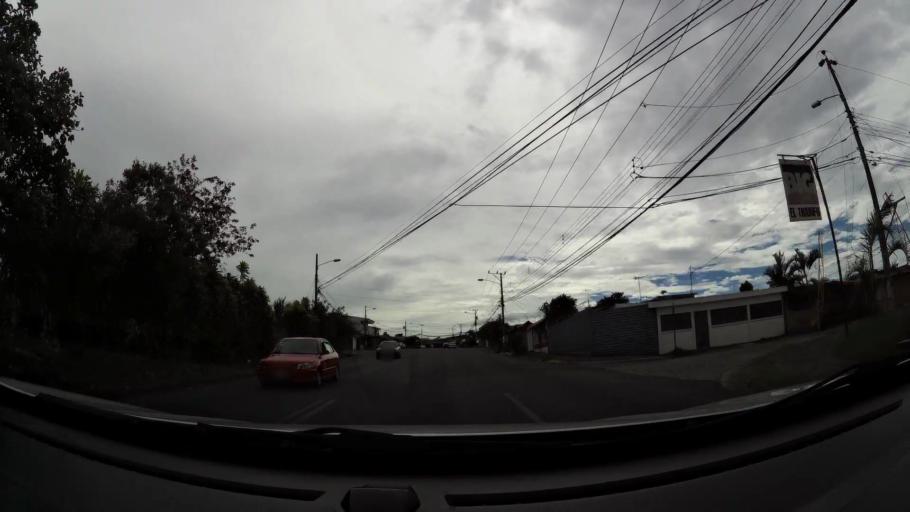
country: CR
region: San Jose
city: Sabanilla
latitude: 9.9520
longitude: -84.0363
